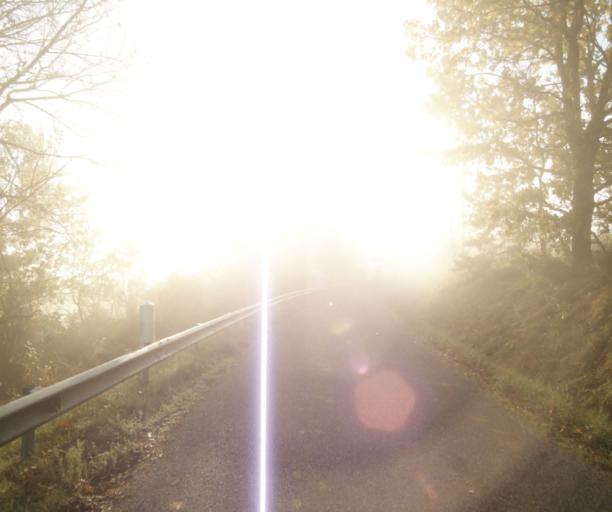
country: FR
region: Midi-Pyrenees
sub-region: Departement de la Haute-Garonne
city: Villemur-sur-Tarn
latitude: 43.8895
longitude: 1.4887
